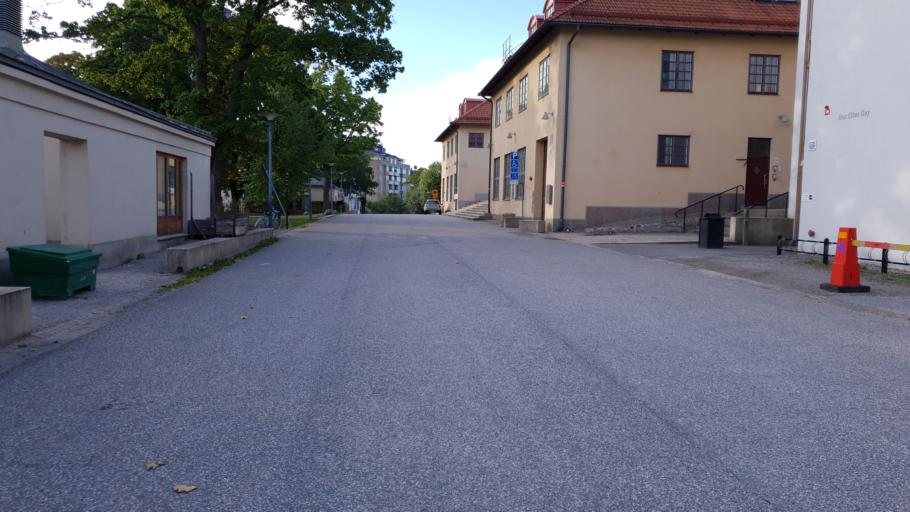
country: SE
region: Stockholm
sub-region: Solna Kommun
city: Solna
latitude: 59.3302
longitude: 18.0133
